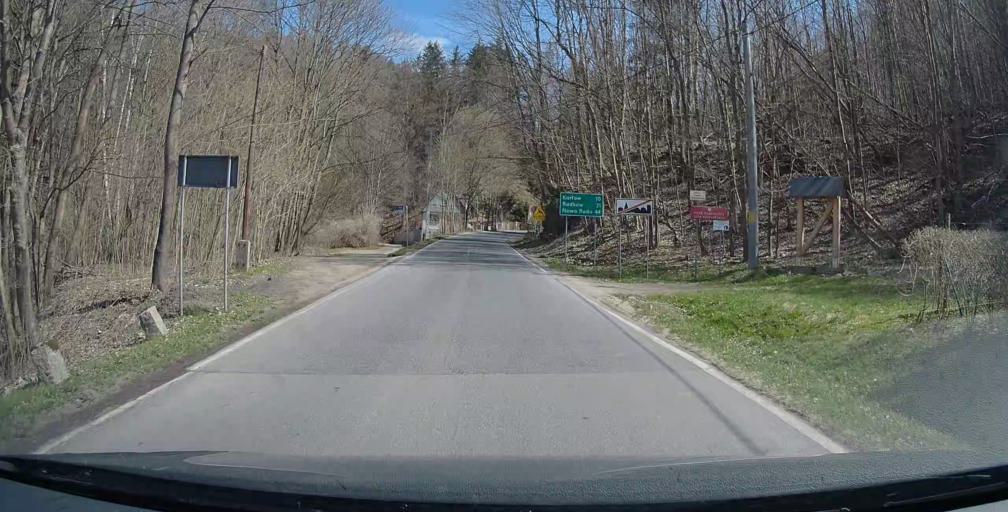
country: PL
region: Lower Silesian Voivodeship
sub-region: Powiat klodzki
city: Kudowa-Zdroj
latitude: 50.4472
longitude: 16.2703
